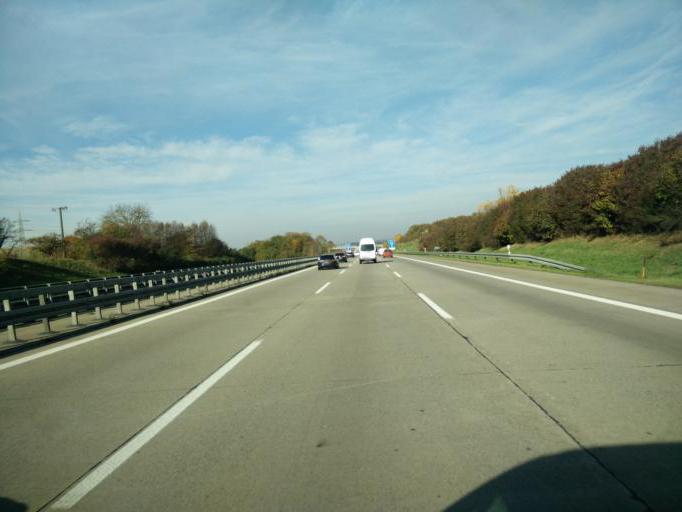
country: DE
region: Baden-Wuerttemberg
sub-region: Regierungsbezirk Stuttgart
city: Denkendorf
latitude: 48.6821
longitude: 9.3304
